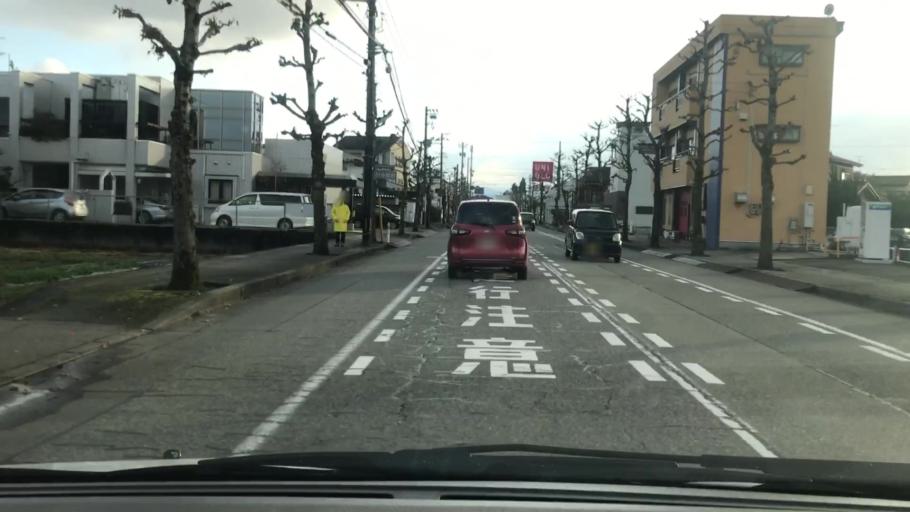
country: JP
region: Toyama
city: Toyama-shi
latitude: 36.6719
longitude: 137.2370
